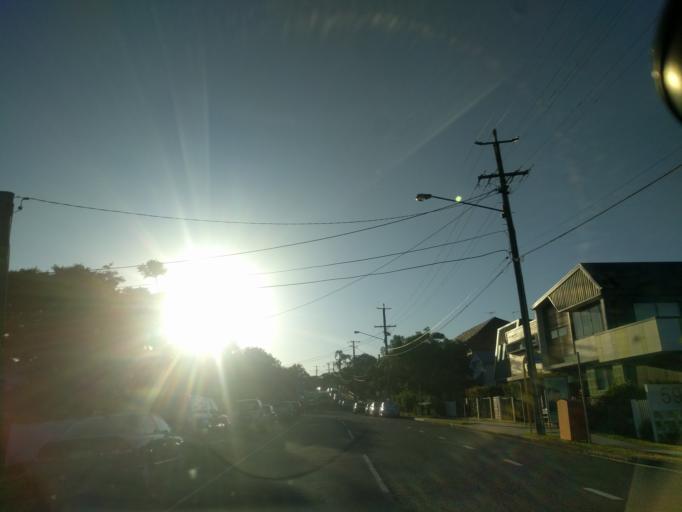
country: AU
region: Queensland
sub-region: Brisbane
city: Wilston
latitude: -27.4457
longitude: 153.0116
